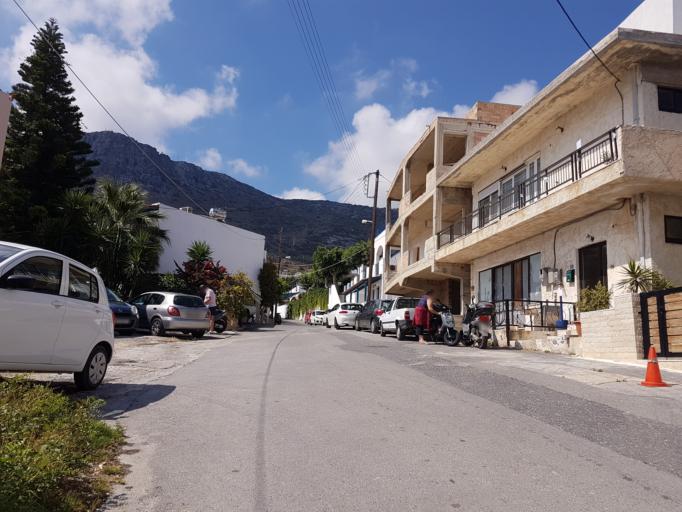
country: GR
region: Crete
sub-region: Nomos Irakleiou
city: Limin Khersonisou
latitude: 35.3104
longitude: 25.3836
